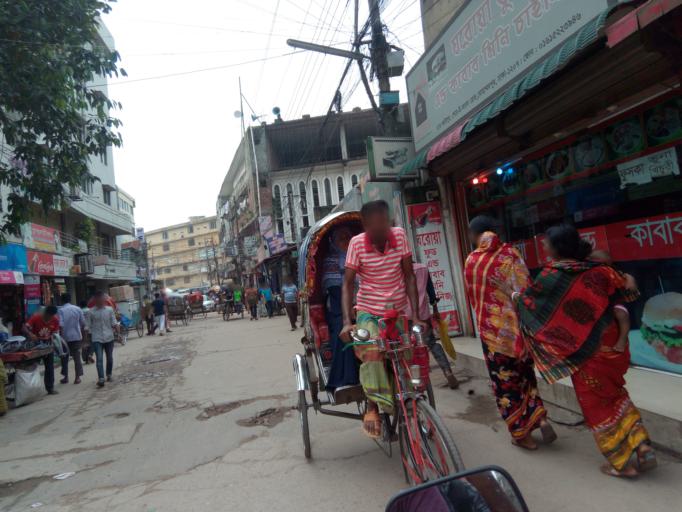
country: BD
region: Dhaka
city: Azimpur
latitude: 23.7563
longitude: 90.3613
